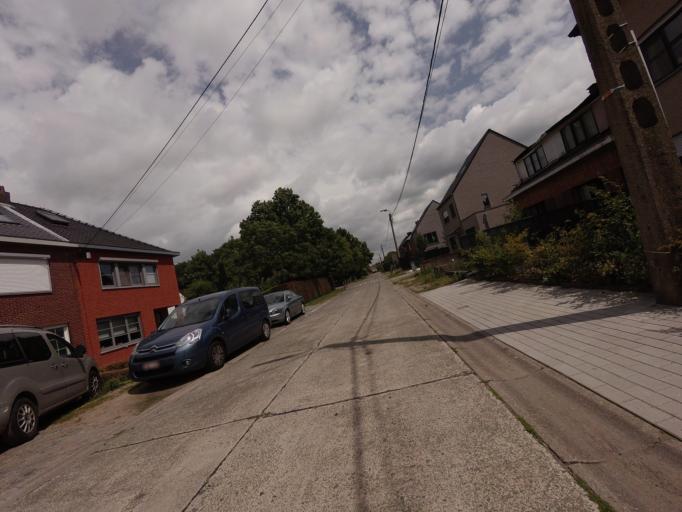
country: BE
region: Flanders
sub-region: Provincie Antwerpen
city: Mechelen
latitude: 51.0467
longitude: 4.4976
